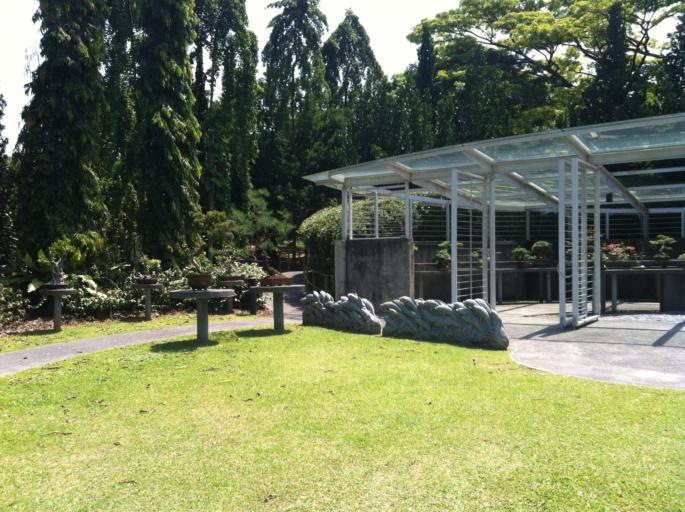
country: SG
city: Singapore
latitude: 1.3098
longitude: 103.8163
